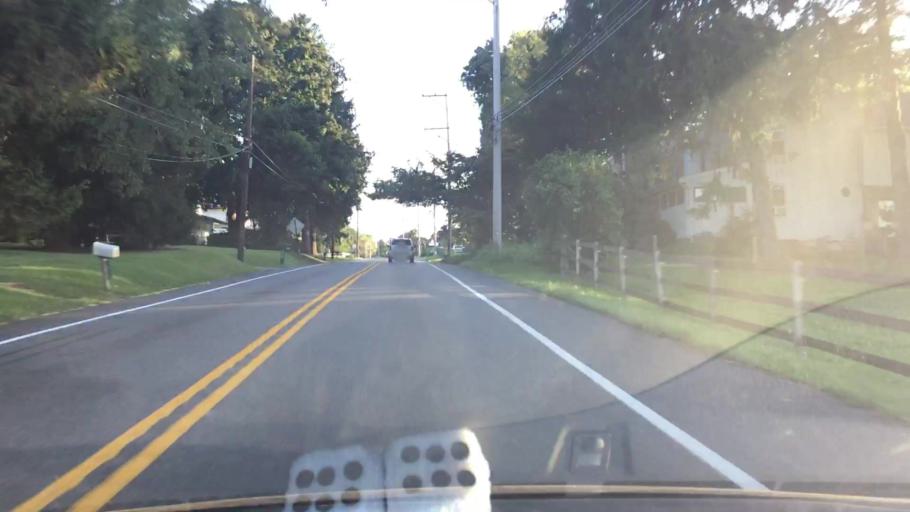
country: US
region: Pennsylvania
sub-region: Delaware County
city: Chester Heights
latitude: 39.8573
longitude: -75.4776
